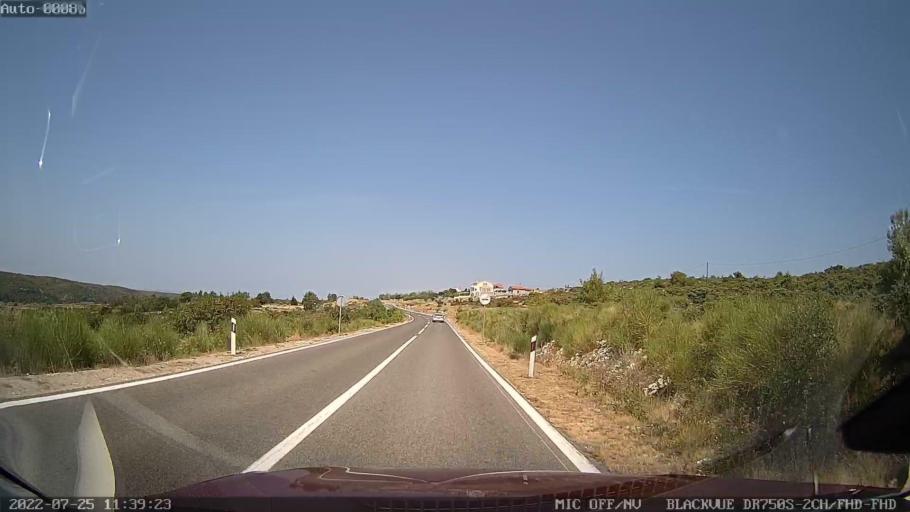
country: HR
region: Zadarska
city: Razanac
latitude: 44.2567
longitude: 15.3721
